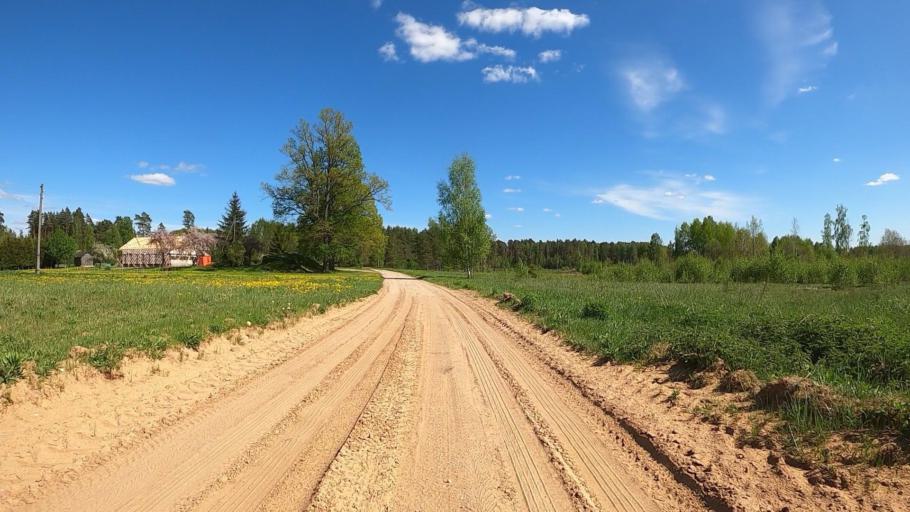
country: LV
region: Salaspils
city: Salaspils
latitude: 56.7916
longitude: 24.3151
